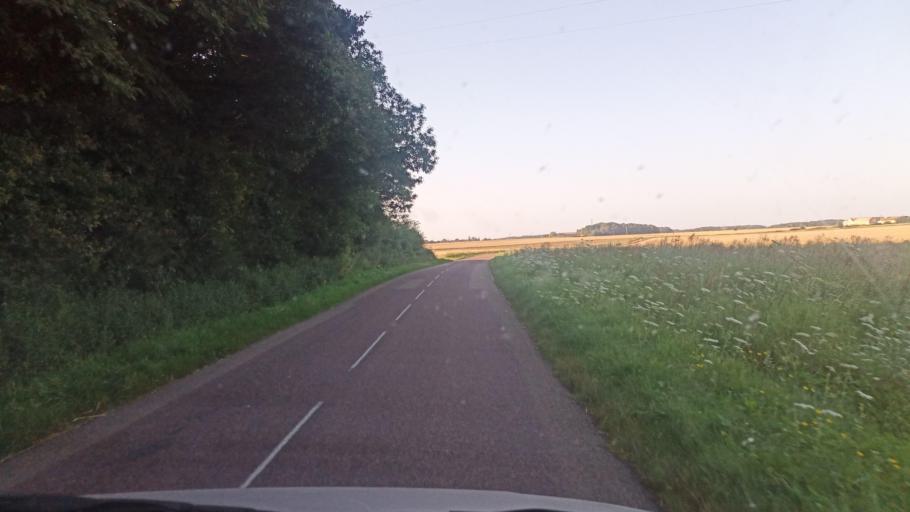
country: FR
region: Bourgogne
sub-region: Departement de l'Yonne
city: Saint-Valerien
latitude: 48.2154
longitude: 3.1226
